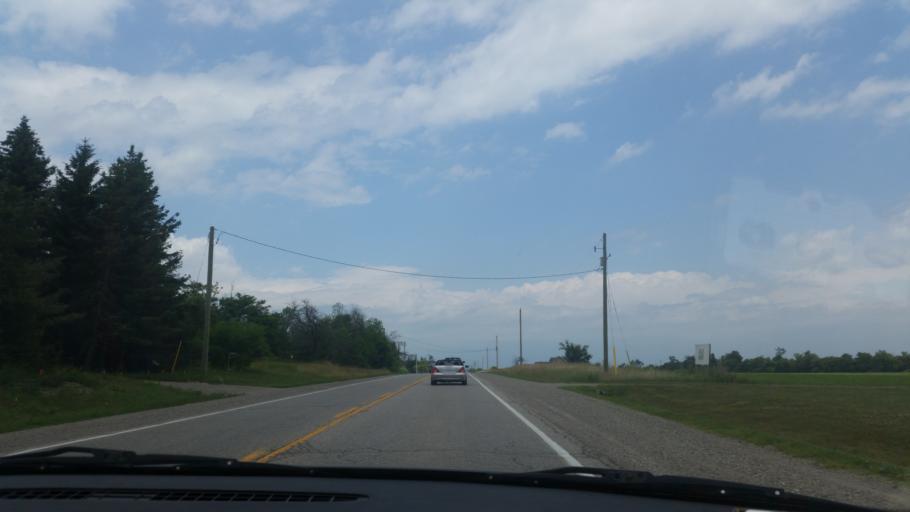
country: CA
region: Ontario
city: Orangeville
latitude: 43.7368
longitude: -80.0870
